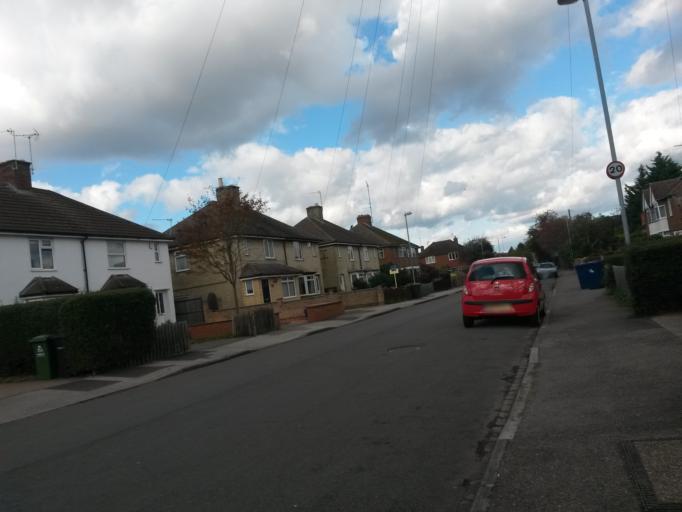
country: GB
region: England
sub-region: Cambridgeshire
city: Cambridge
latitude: 52.2198
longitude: 0.1182
